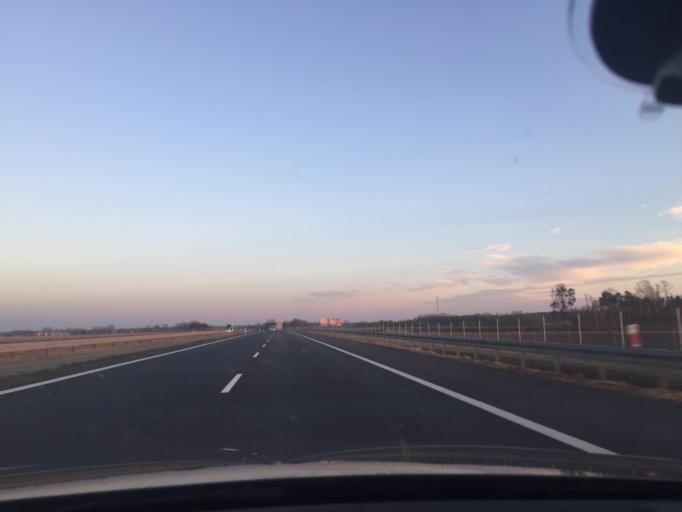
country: PL
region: Lodz Voivodeship
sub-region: Powiat poddebicki
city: Wartkowice
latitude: 51.9805
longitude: 19.0719
